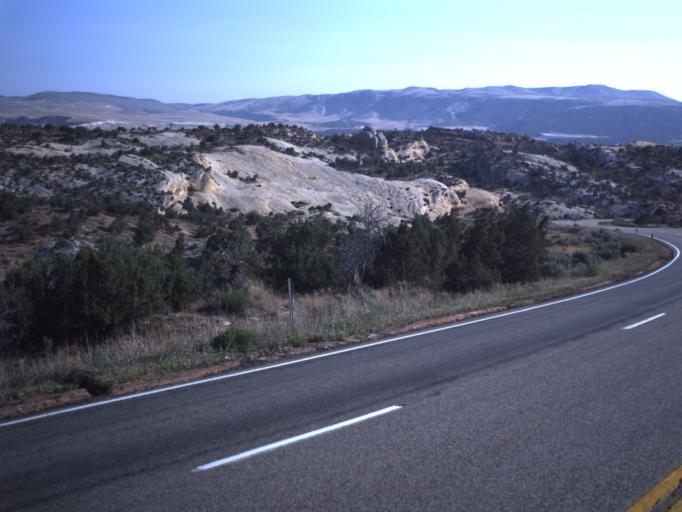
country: US
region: Utah
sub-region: Uintah County
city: Vernal
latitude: 40.5808
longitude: -109.4745
